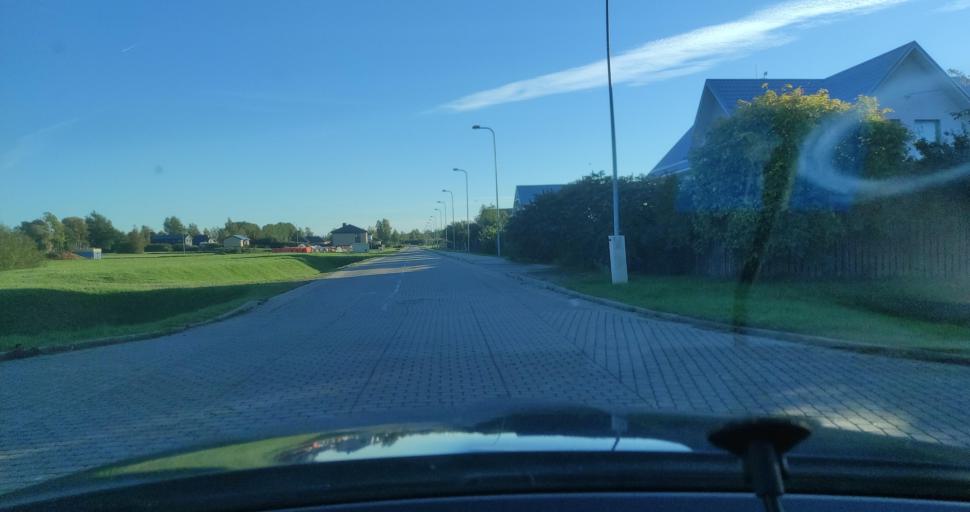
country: LV
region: Ventspils
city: Ventspils
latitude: 57.3692
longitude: 21.5750
